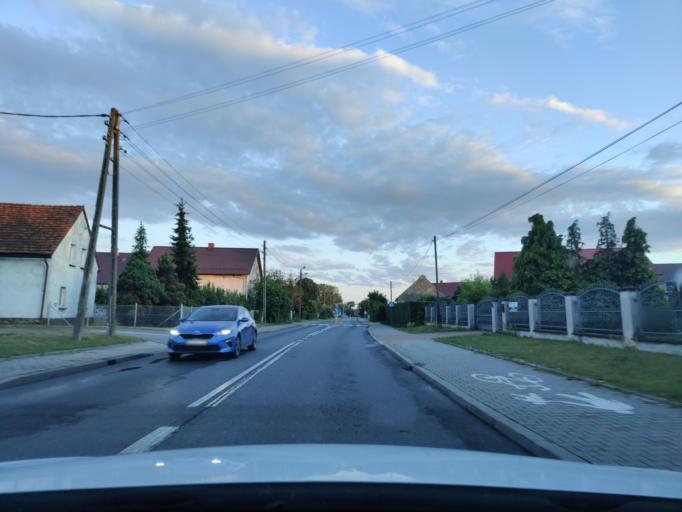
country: PL
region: Opole Voivodeship
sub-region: Powiat brzeski
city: Grodkow
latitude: 50.6585
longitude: 17.3891
